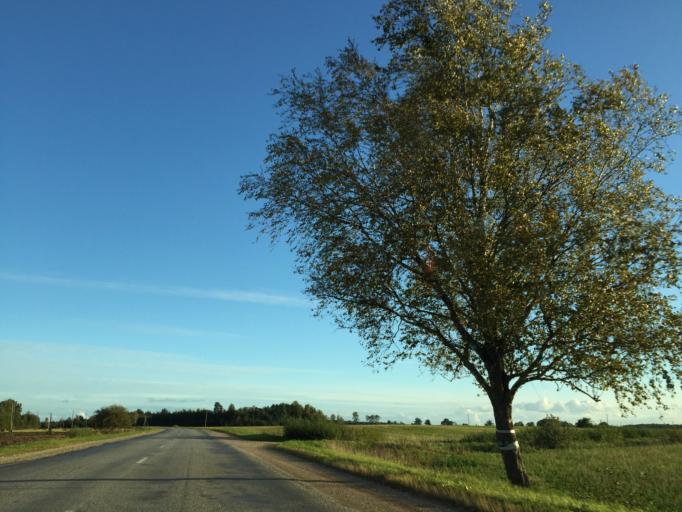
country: LV
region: Saldus Rajons
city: Saldus
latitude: 56.7361
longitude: 22.3773
